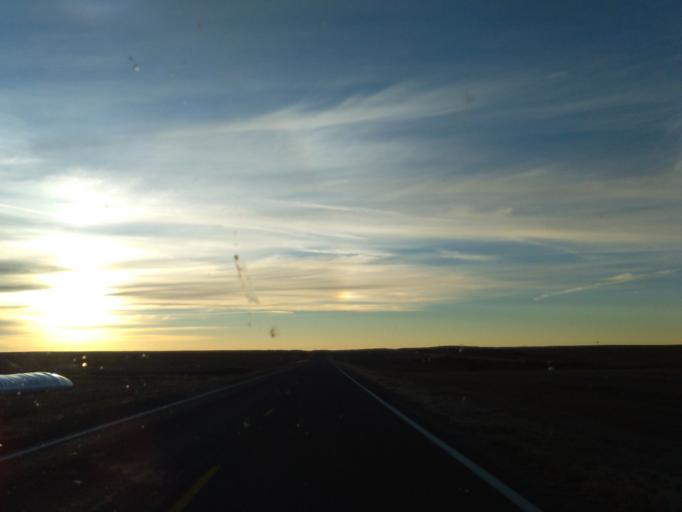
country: US
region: Kansas
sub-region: Thomas County
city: Colby
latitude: 39.0332
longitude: -101.2830
